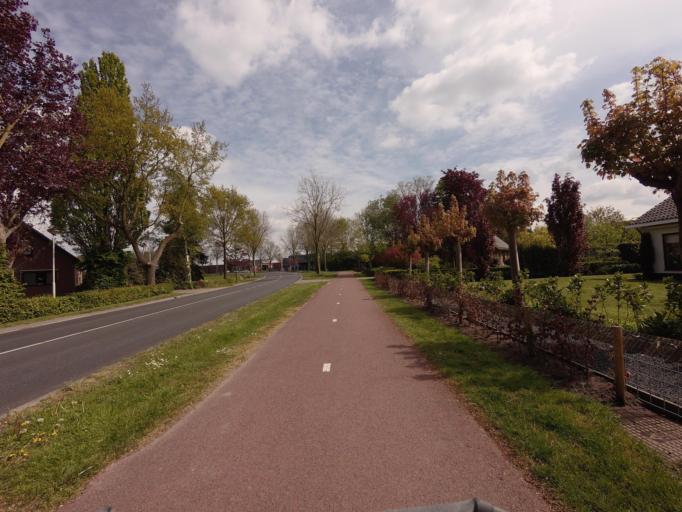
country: NL
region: Utrecht
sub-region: Gemeente Montfoort
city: Montfoort
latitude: 52.0463
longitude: 4.9352
